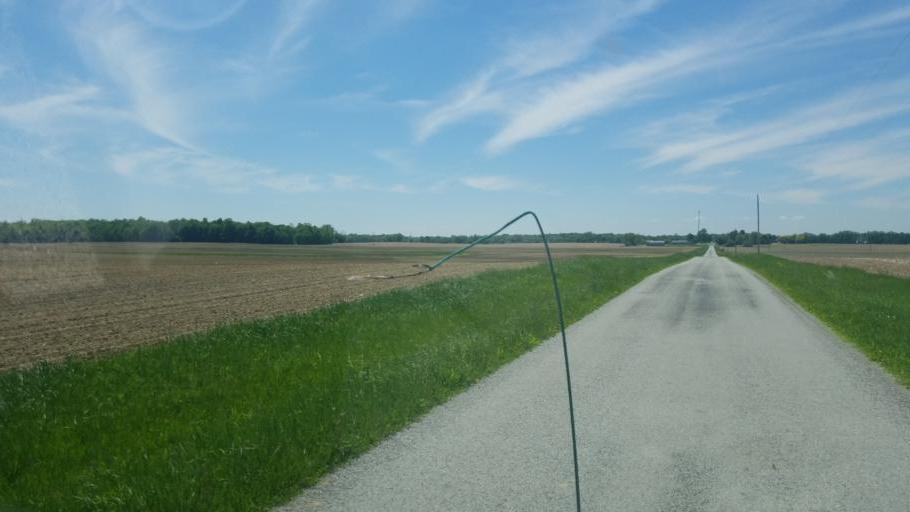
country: US
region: Ohio
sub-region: Huron County
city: Greenwich
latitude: 41.1191
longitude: -82.5894
